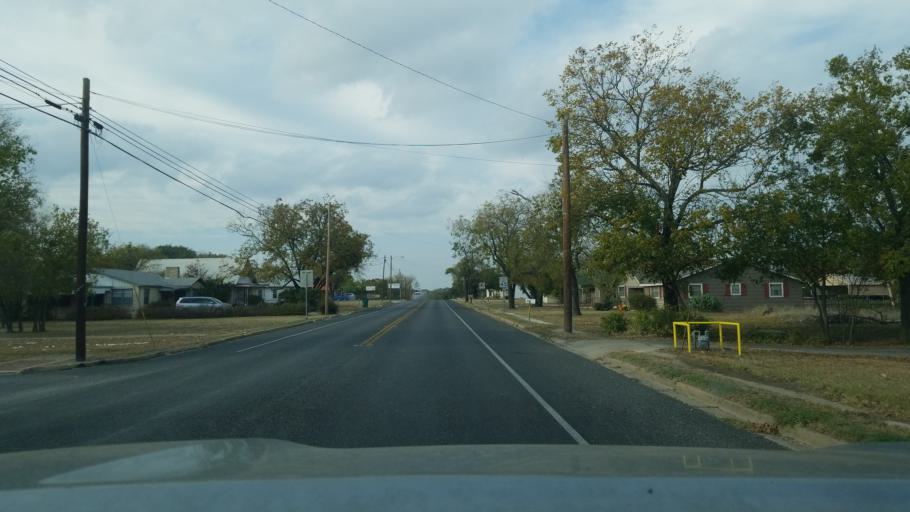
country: US
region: Texas
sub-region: Mills County
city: Goldthwaite
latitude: 31.4588
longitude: -98.5728
